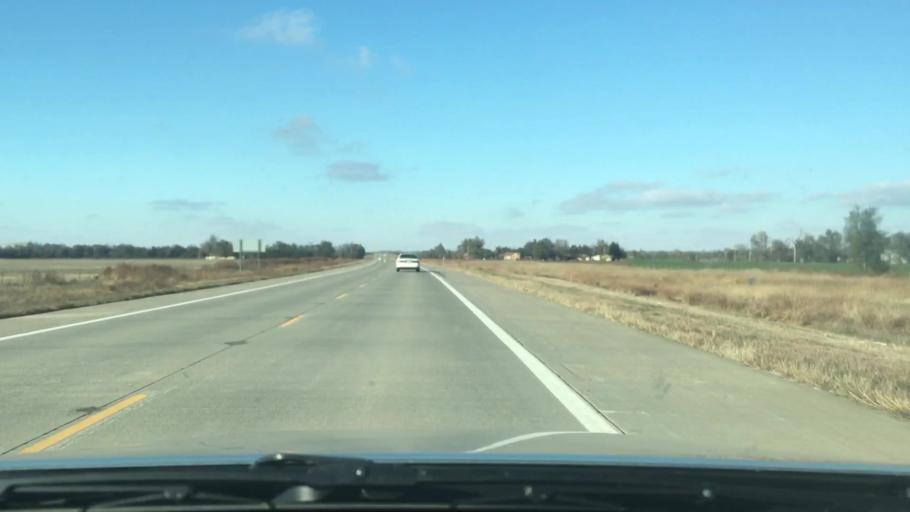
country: US
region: Kansas
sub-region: Reno County
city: Hutchinson
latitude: 38.0665
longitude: -97.9862
